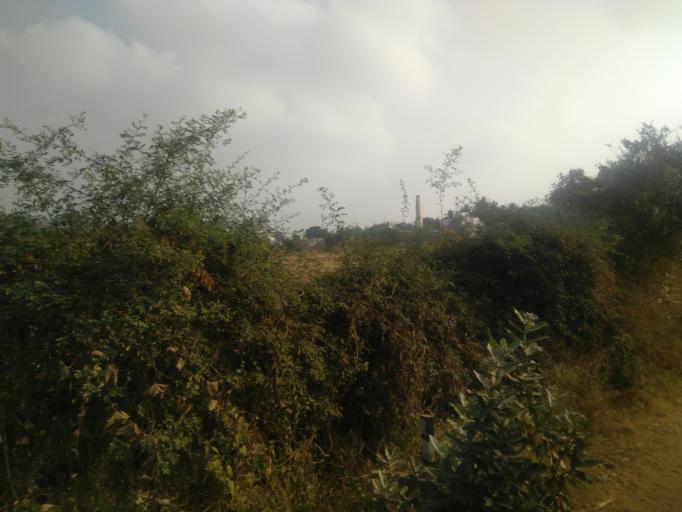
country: IN
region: Tamil Nadu
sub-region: Coimbatore
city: Perur
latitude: 11.0545
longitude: 76.9001
